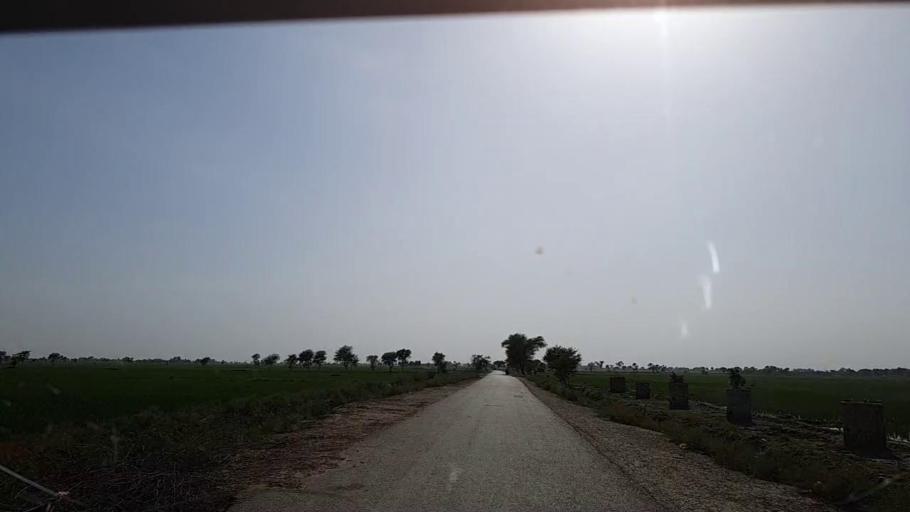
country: PK
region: Sindh
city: Phulji
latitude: 26.9887
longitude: 67.6618
